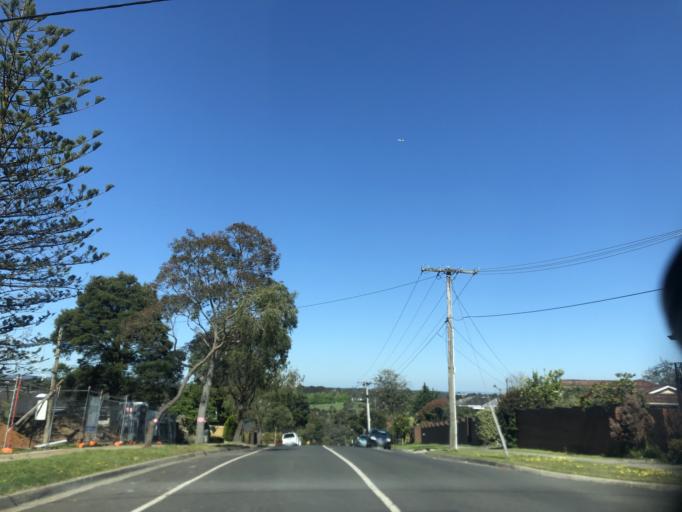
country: AU
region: Victoria
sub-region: Monash
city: Notting Hill
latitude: -37.8988
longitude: 145.1479
